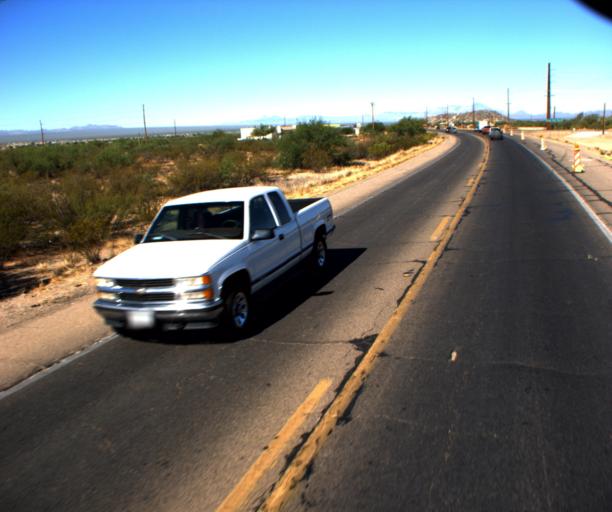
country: US
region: Arizona
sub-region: Pima County
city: Tucson Estates
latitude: 32.1648
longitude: -111.0950
